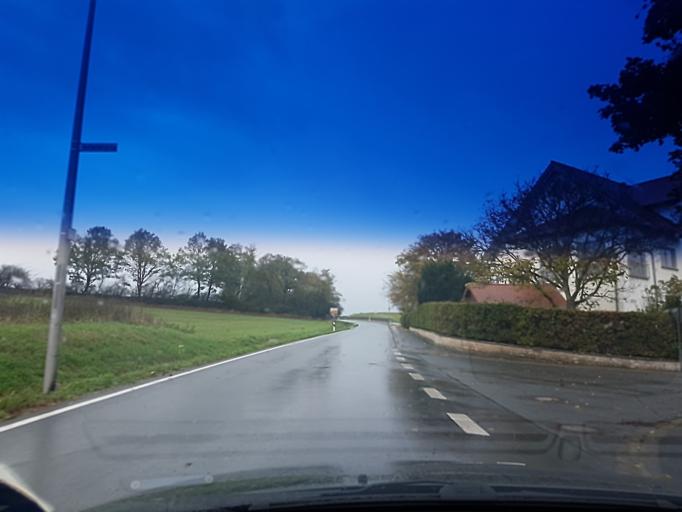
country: DE
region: Bavaria
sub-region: Regierungsbezirk Mittelfranken
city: Wachenroth
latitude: 49.7462
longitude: 10.6675
